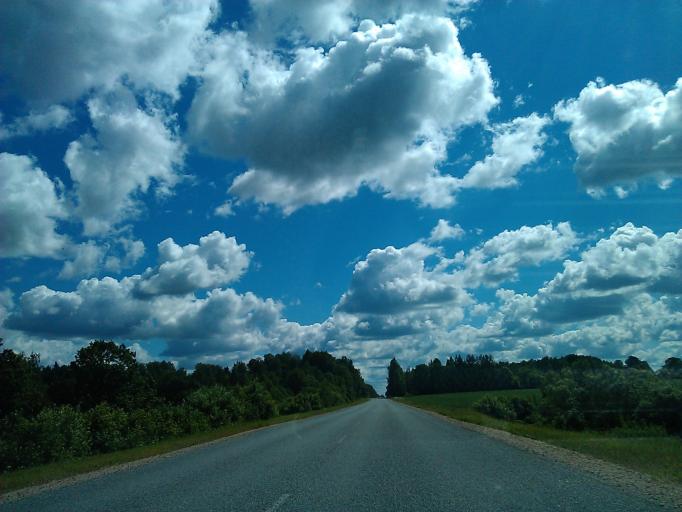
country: LV
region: Madonas Rajons
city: Madona
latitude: 56.8348
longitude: 26.2900
